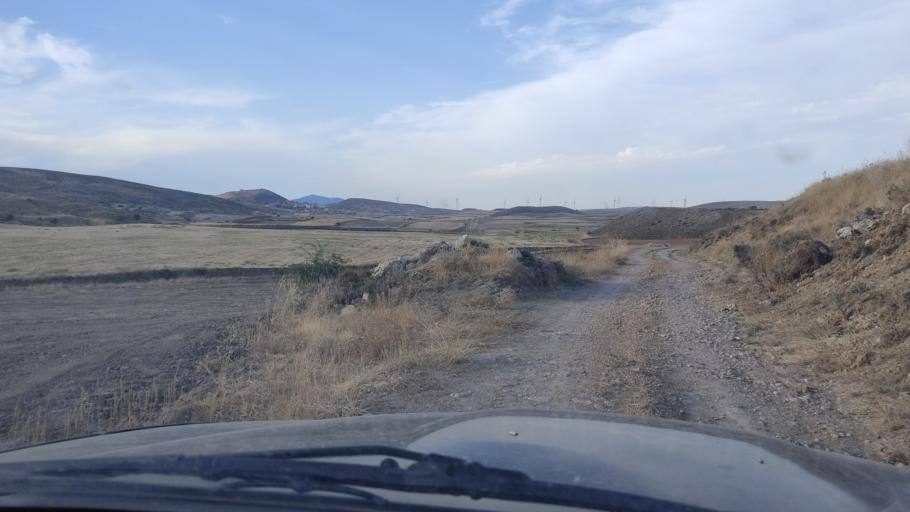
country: ES
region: Aragon
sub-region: Provincia de Teruel
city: Monforte de Moyuela
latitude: 41.0349
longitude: -0.9979
